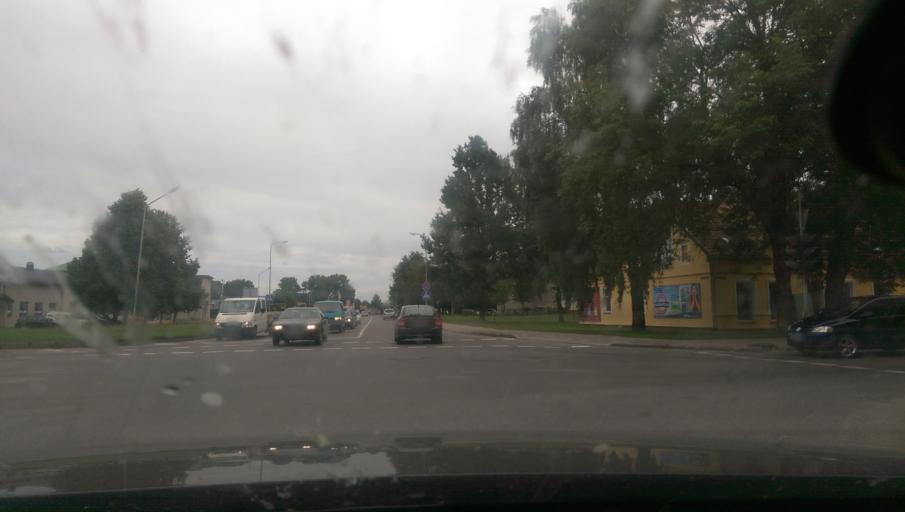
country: LT
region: Klaipedos apskritis
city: Silute
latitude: 55.3477
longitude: 21.4705
